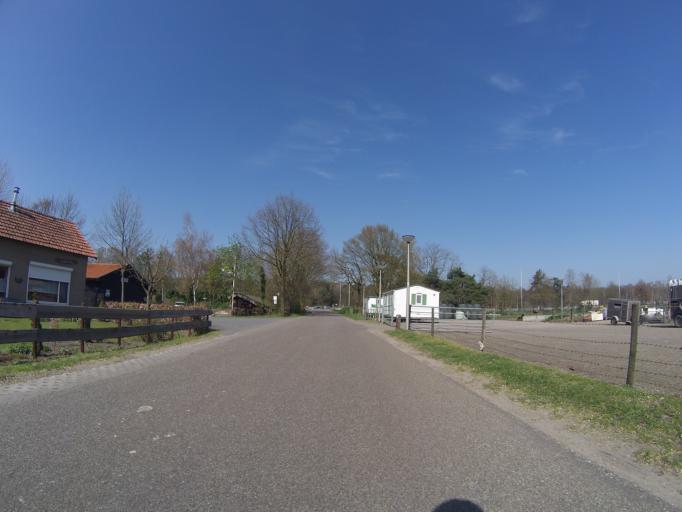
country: NL
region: Utrecht
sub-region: Gemeente Utrechtse Heuvelrug
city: Maarsbergen
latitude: 52.0513
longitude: 5.4215
